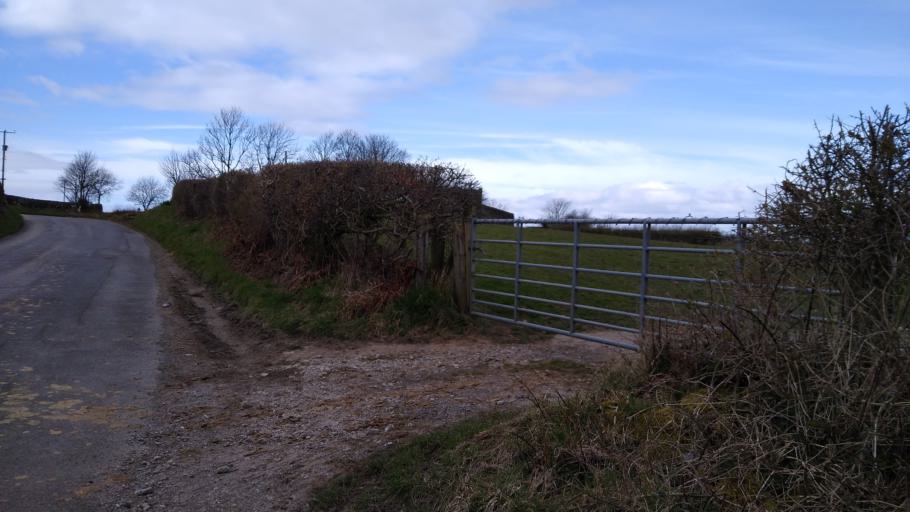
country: GB
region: England
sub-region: Cumbria
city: Dearham
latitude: 54.6920
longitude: -3.4455
